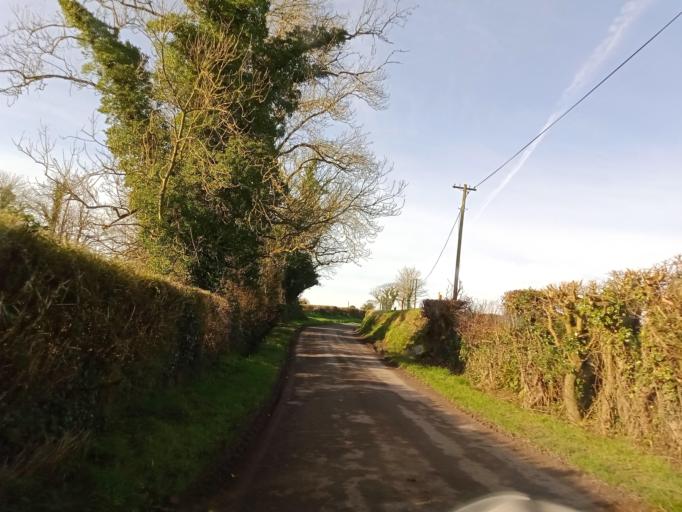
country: IE
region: Munster
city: Fethard
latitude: 52.5613
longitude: -7.5889
